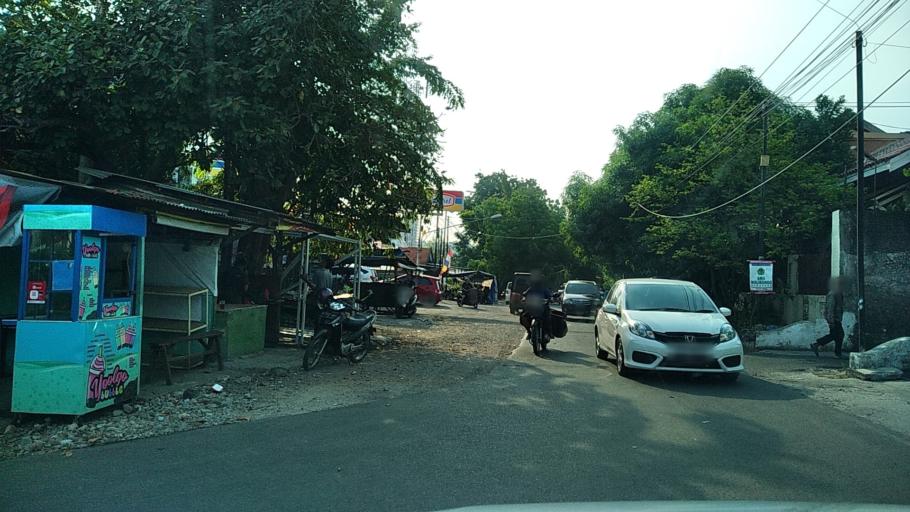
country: ID
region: Central Java
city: Semarang
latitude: -7.0006
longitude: 110.4313
